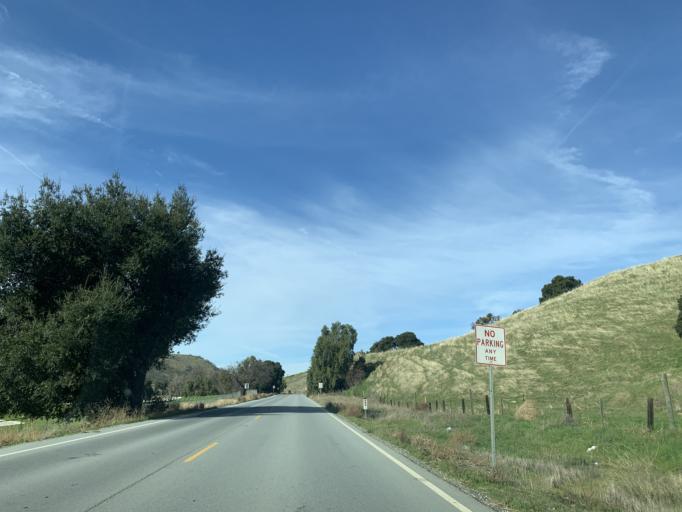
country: US
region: California
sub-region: San Benito County
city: Ridgemark
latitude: 36.7688
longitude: -121.3028
